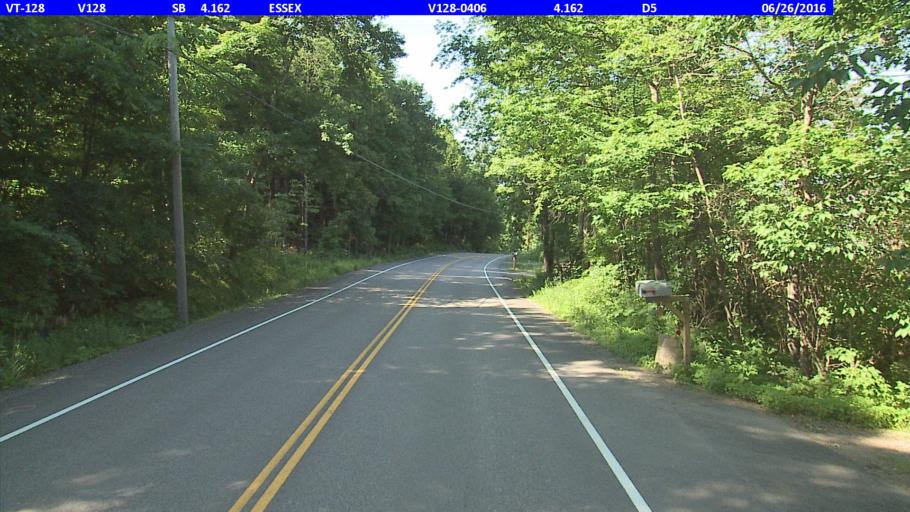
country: US
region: Vermont
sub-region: Chittenden County
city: Jericho
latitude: 44.5563
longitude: -73.0311
